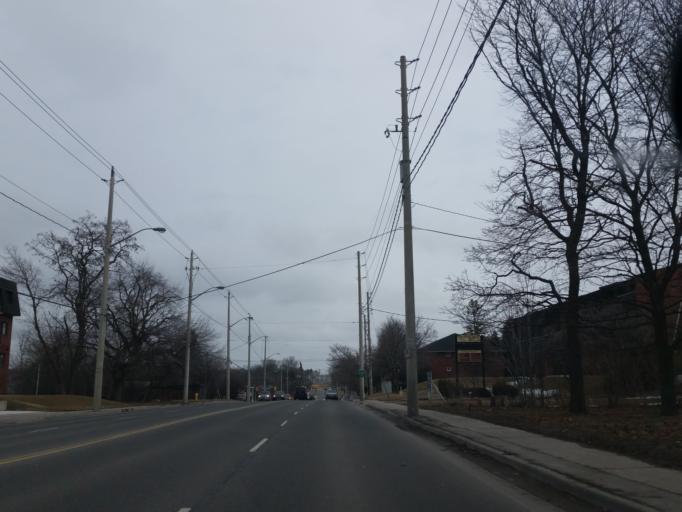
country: CA
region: Ontario
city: Oshawa
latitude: 43.8814
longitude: -78.9351
